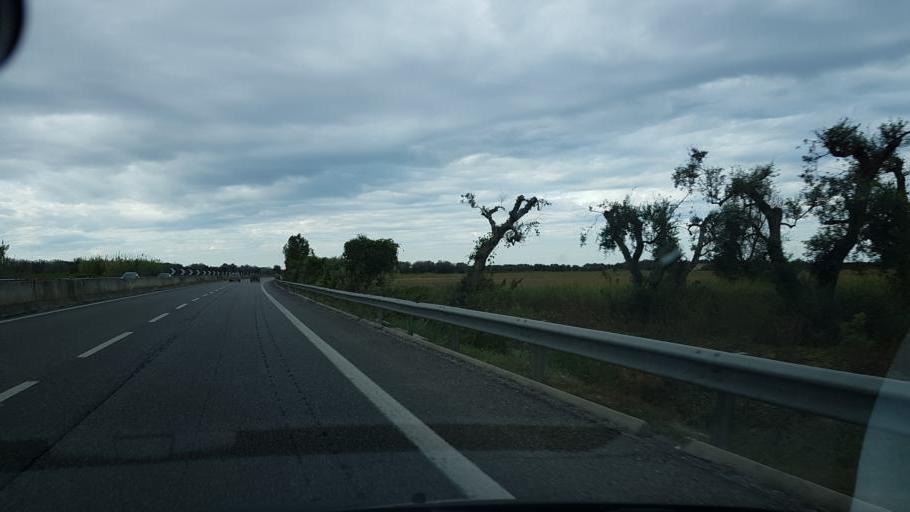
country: IT
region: Apulia
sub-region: Provincia di Brindisi
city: San Pietro Vernotico
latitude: 40.5225
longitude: 18.0157
